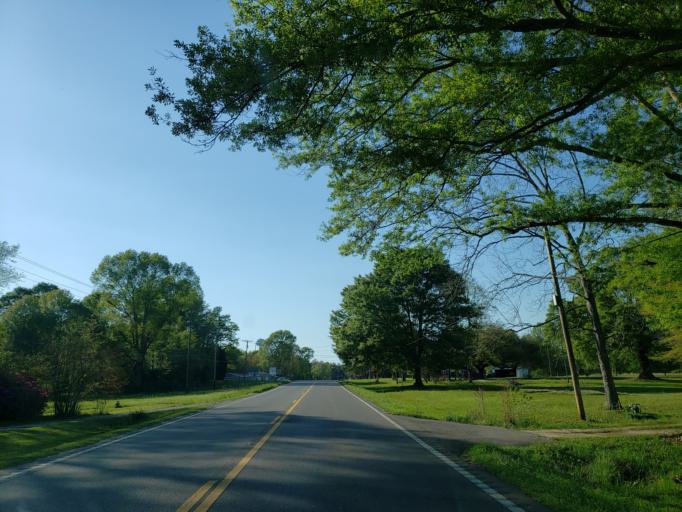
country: US
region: Mississippi
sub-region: Jones County
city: Laurel
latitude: 31.6500
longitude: -89.1026
